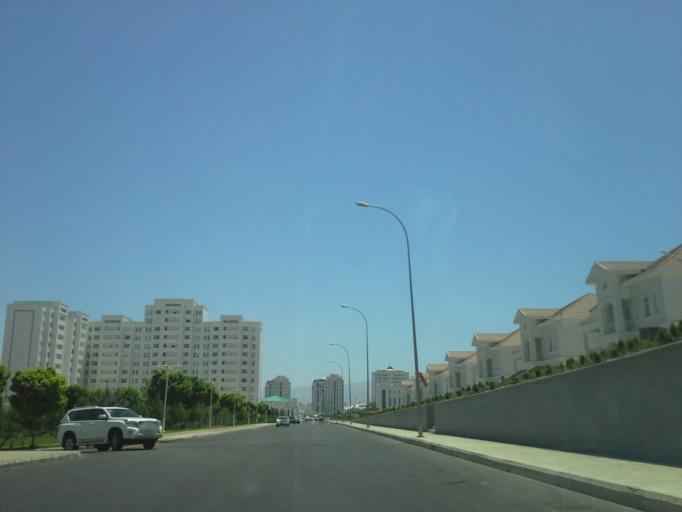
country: TM
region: Ahal
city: Ashgabat
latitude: 37.9333
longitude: 58.3646
